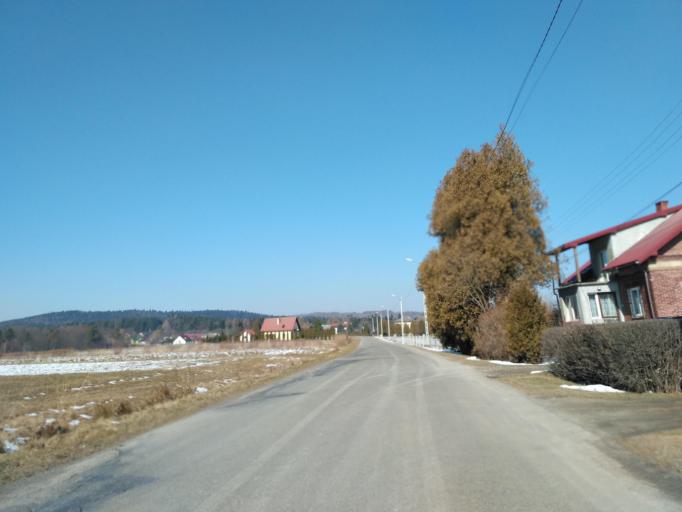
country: PL
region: Subcarpathian Voivodeship
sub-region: Powiat brzozowski
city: Jasienica Rosielna
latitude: 49.7682
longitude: 21.9222
